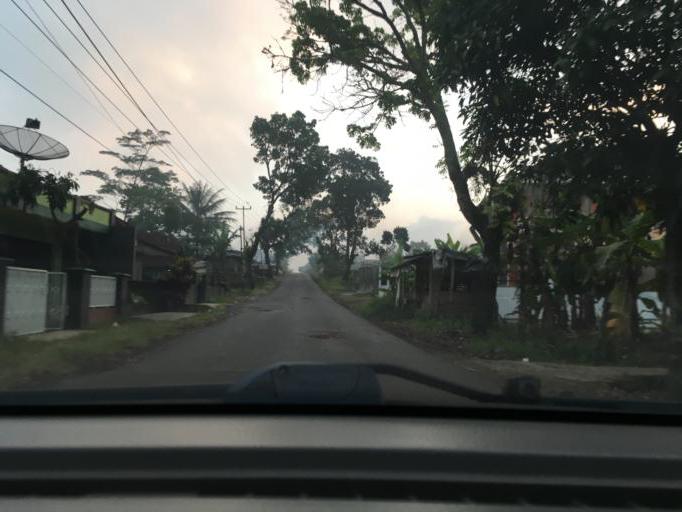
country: ID
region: West Java
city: Pasirtamiang
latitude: -7.2125
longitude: 108.1998
